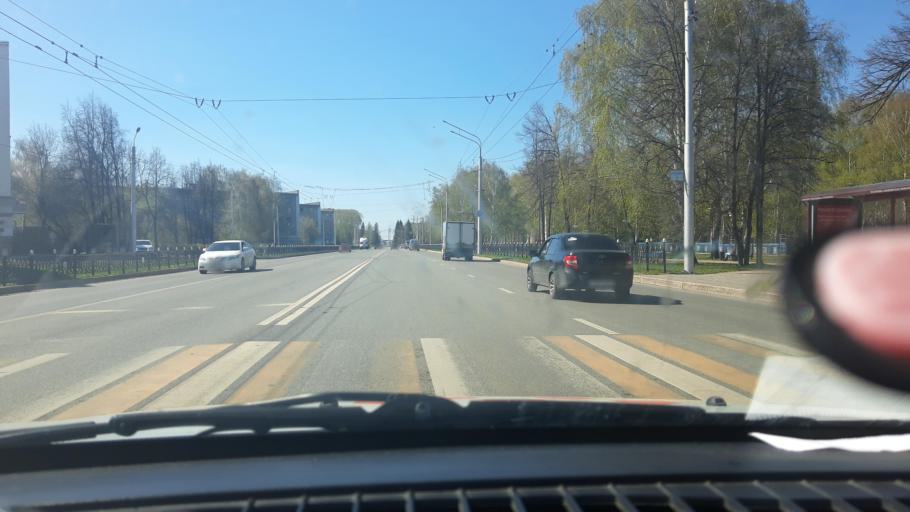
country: RU
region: Bashkortostan
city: Sterlitamak
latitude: 53.6356
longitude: 55.9156
